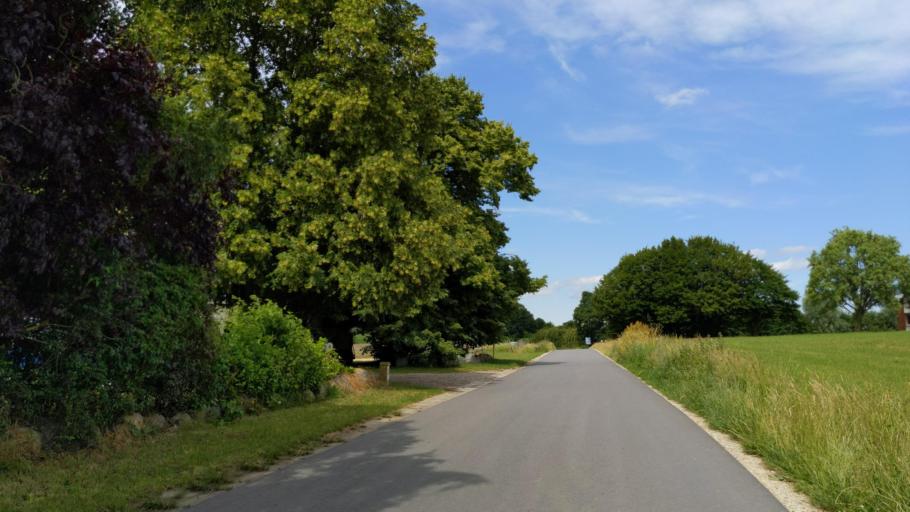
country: DE
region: Schleswig-Holstein
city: Kasseedorf
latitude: 54.1196
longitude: 10.7072
